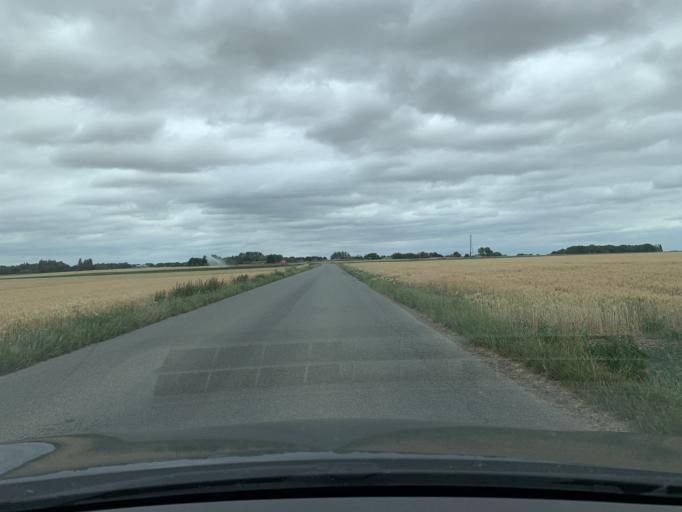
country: FR
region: Nord-Pas-de-Calais
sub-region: Departement du Nord
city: Raillencourt-Sainte-Olle
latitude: 50.2018
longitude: 3.1408
